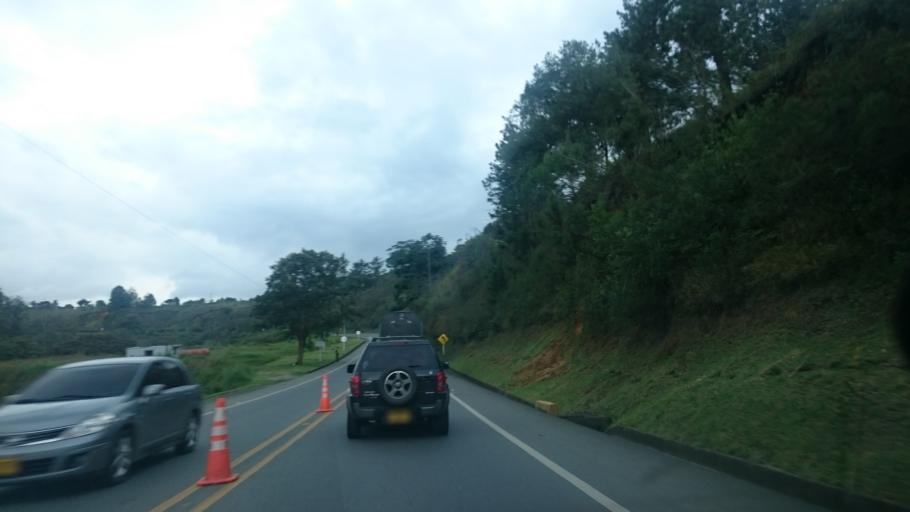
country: CO
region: Cauca
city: Cajibio
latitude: 2.5539
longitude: -76.5666
